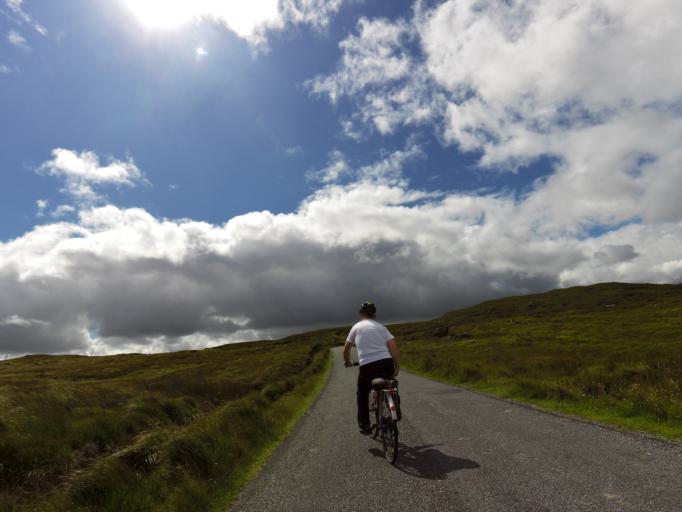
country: IE
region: Connaught
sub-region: County Galway
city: Oughterard
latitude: 53.3962
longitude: -9.3348
